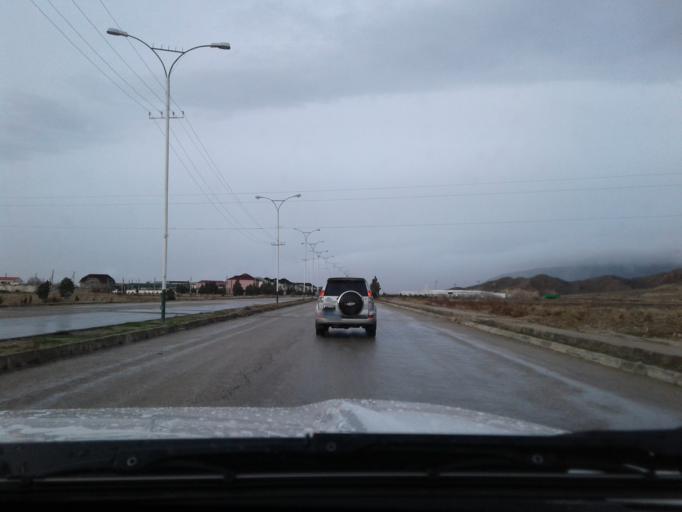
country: TM
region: Balkan
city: Balkanabat
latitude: 39.5316
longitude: 54.3544
